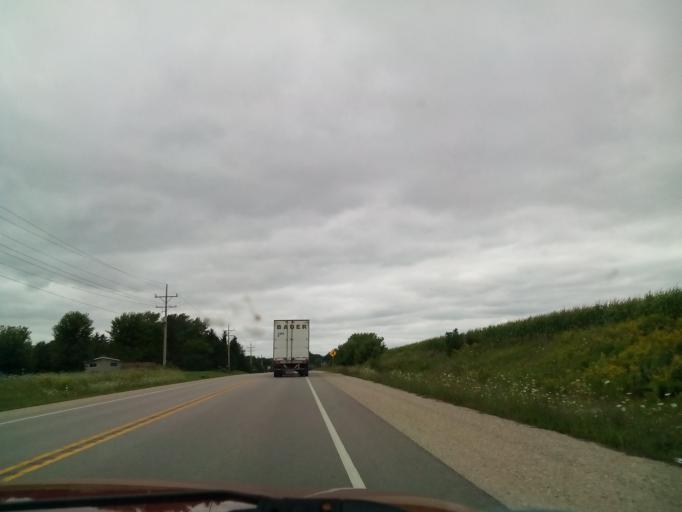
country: US
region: Wisconsin
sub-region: Outagamie County
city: Hortonville
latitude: 44.2726
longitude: -88.6938
